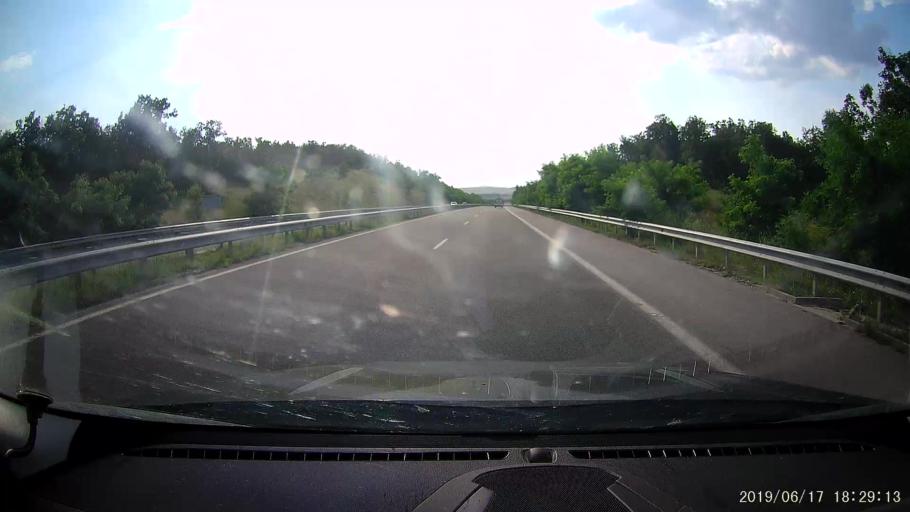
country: BG
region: Khaskovo
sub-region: Obshtina Dimitrovgrad
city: Dimitrovgrad
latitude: 42.0273
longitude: 25.5604
